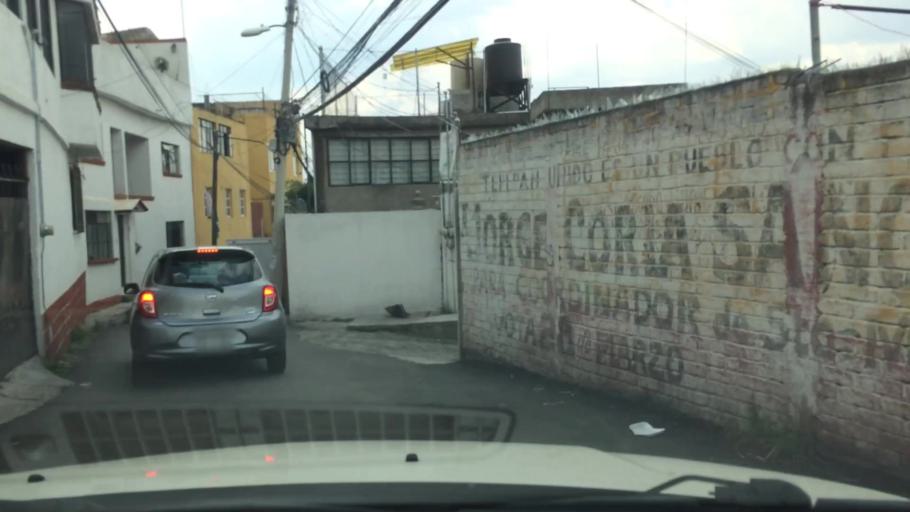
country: MX
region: Mexico City
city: Tlalpan
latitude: 19.2780
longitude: -99.1375
